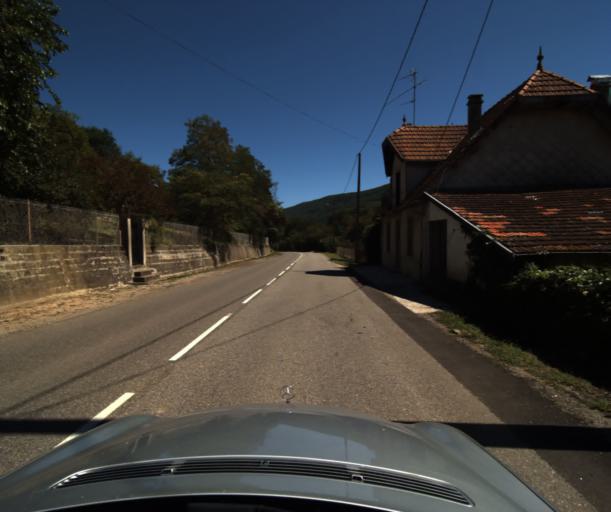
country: FR
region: Midi-Pyrenees
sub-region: Departement de l'Ariege
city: Lavelanet
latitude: 42.9562
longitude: 1.9025
